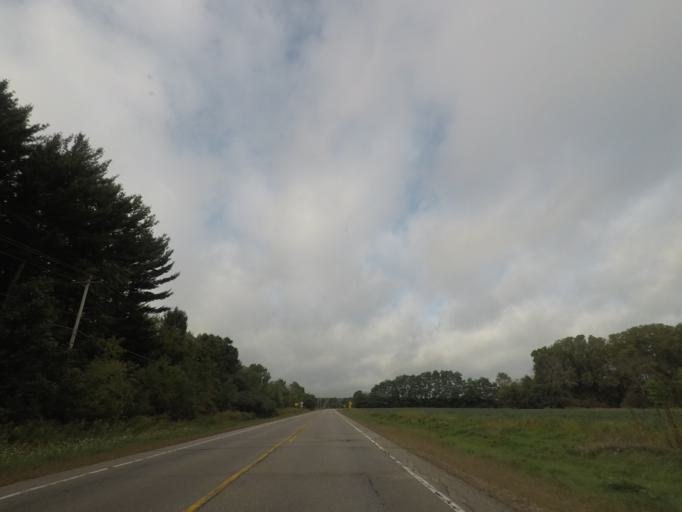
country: US
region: Wisconsin
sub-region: Waukesha County
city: Dousman
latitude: 43.0278
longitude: -88.5138
